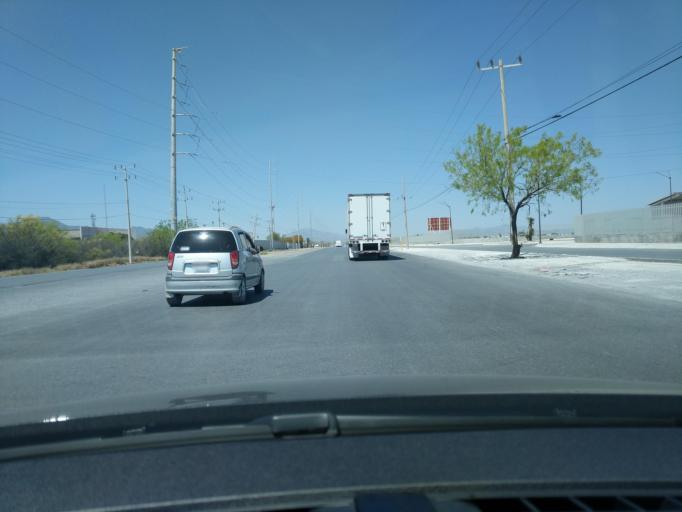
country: MX
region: Nuevo Leon
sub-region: Salinas Victoria
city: Emiliano Zapata
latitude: 25.8995
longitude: -100.2622
